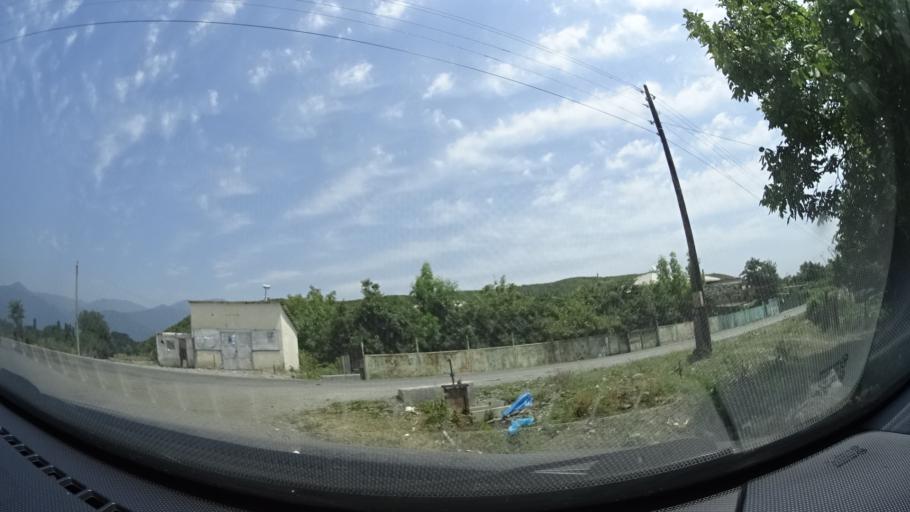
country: GE
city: Bagdadi
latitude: 41.8119
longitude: 46.1410
